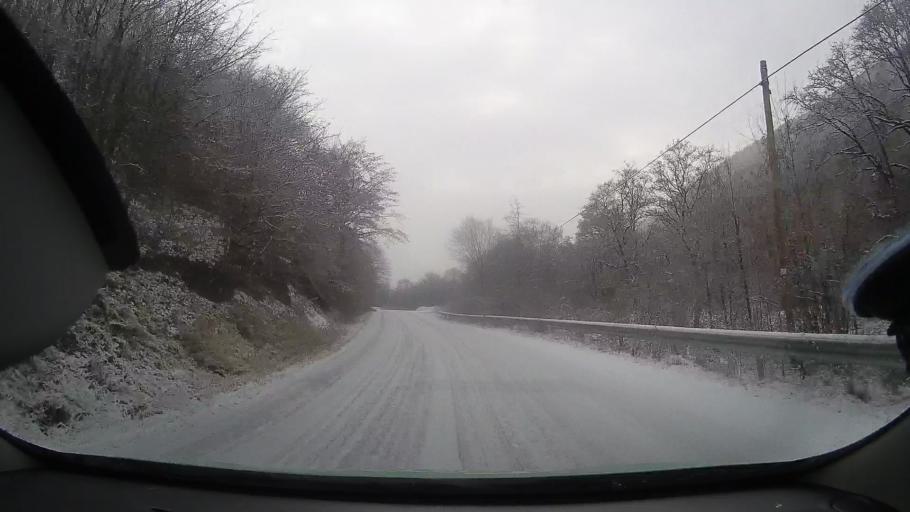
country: RO
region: Alba
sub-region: Comuna Rimetea
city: Rimetea
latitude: 46.4924
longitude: 23.5794
